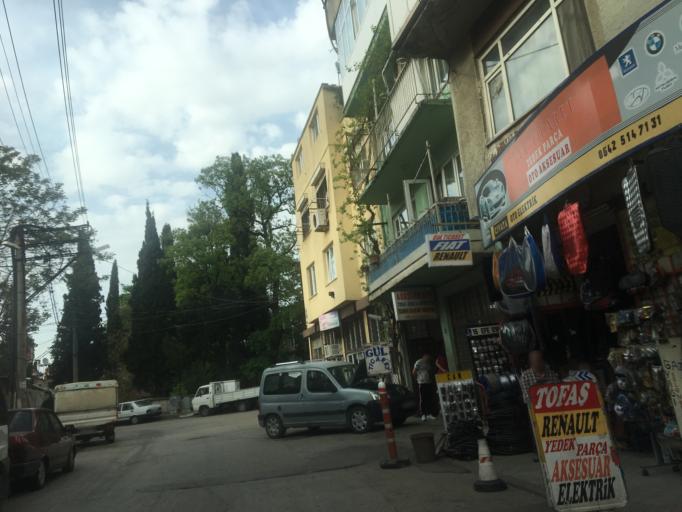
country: TR
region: Bursa
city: Yildirim
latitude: 40.2017
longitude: 29.0458
